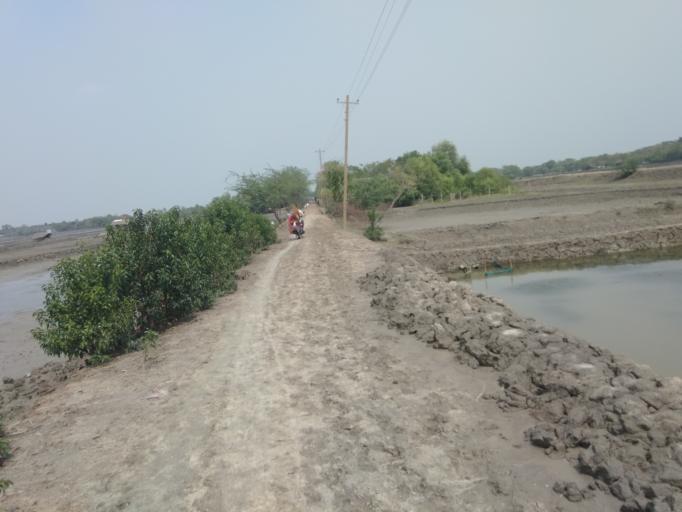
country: IN
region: West Bengal
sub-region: North 24 Parganas
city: Taki
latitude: 22.2769
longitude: 89.2843
